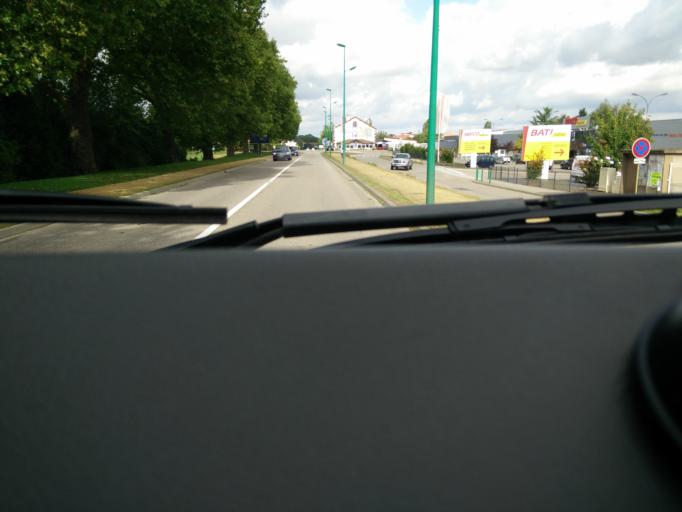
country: FR
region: Lorraine
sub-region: Departement de la Meuse
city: Verdun
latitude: 49.1471
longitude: 5.4044
